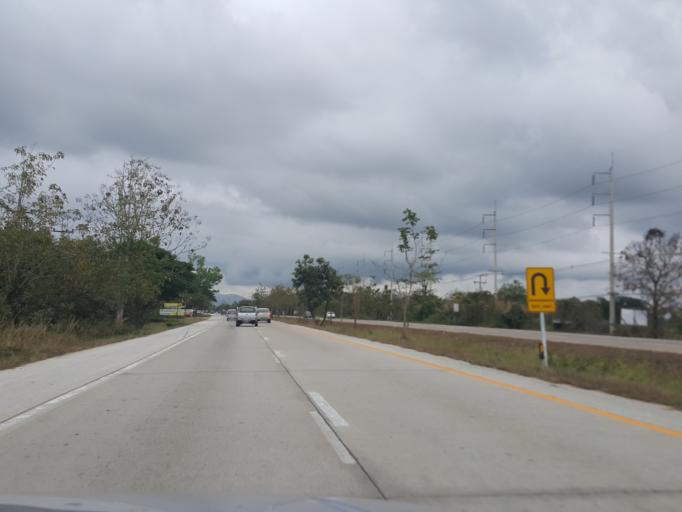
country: TH
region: Lampang
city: Lampang
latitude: 18.2925
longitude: 99.4243
